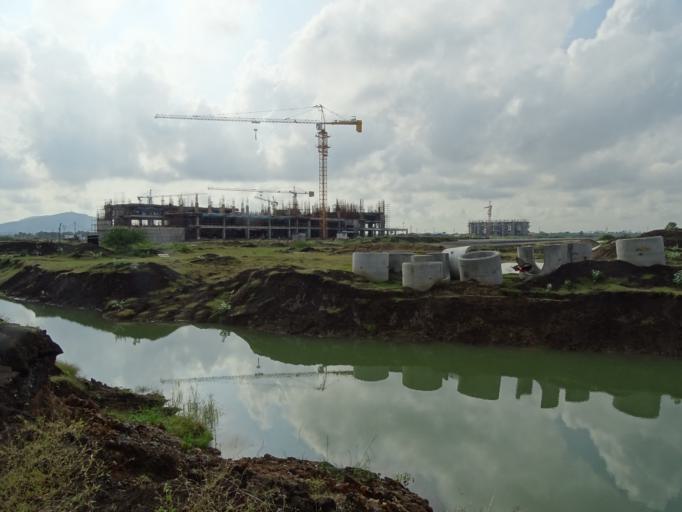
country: IN
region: Andhra Pradesh
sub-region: Guntur
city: Mangalagiri
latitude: 16.4596
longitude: 80.5331
